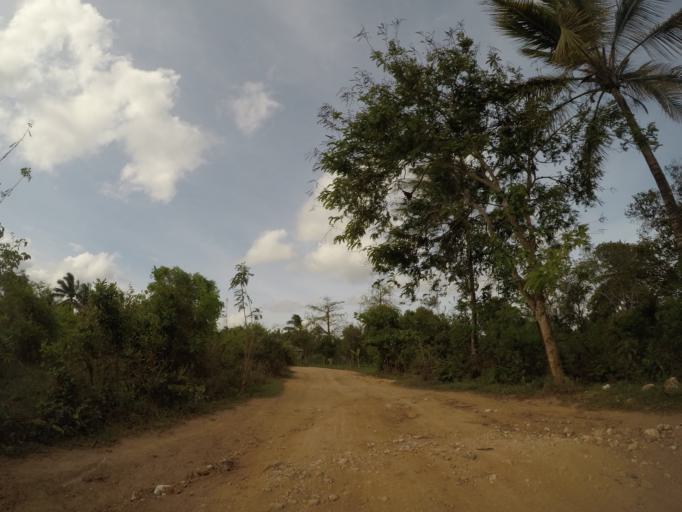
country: TZ
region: Zanzibar Central/South
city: Koani
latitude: -6.2294
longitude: 39.3193
